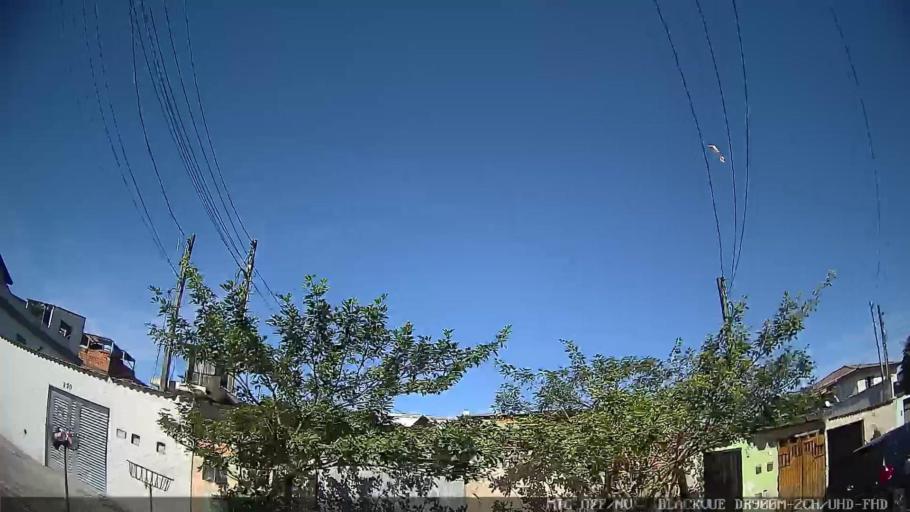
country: BR
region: Sao Paulo
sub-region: Guaruja
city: Guaruja
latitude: -23.9654
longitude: -46.2795
